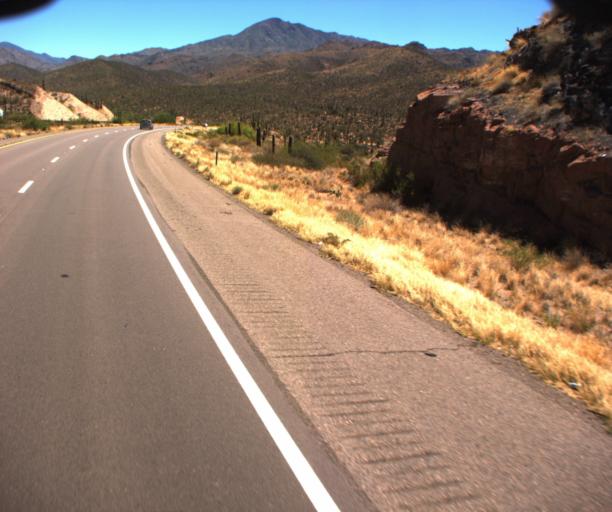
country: US
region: Arizona
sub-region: Maricopa County
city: Rio Verde
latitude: 33.7492
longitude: -111.5025
